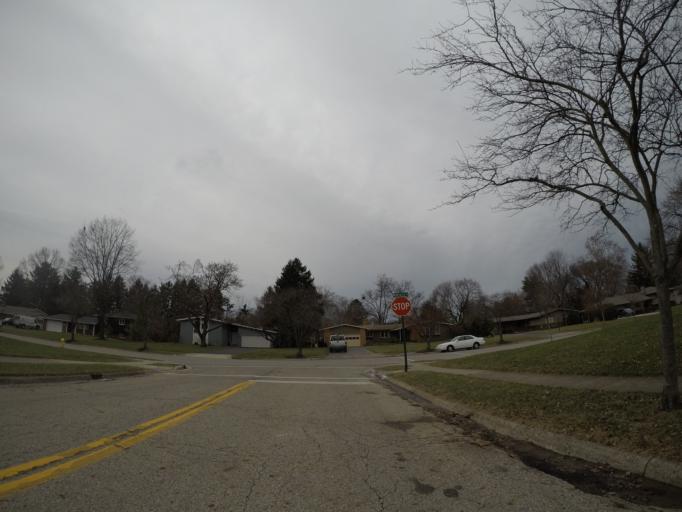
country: US
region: Ohio
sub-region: Franklin County
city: Upper Arlington
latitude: 40.0394
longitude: -83.0842
